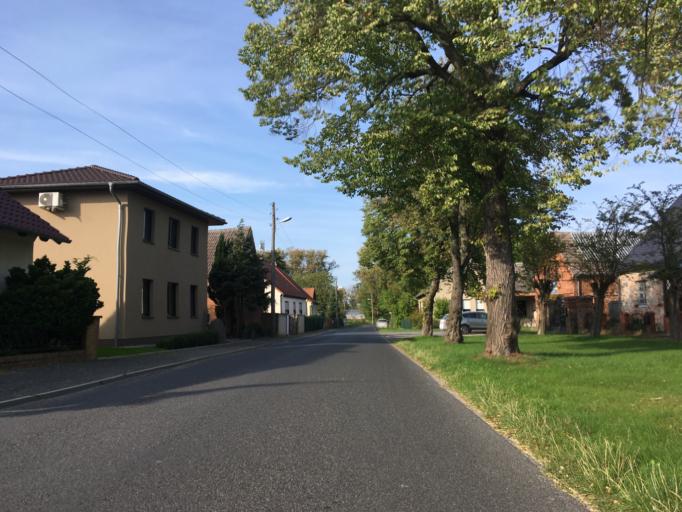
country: DE
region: Brandenburg
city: Brieskow-Finkenheerd
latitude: 52.2908
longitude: 14.5512
